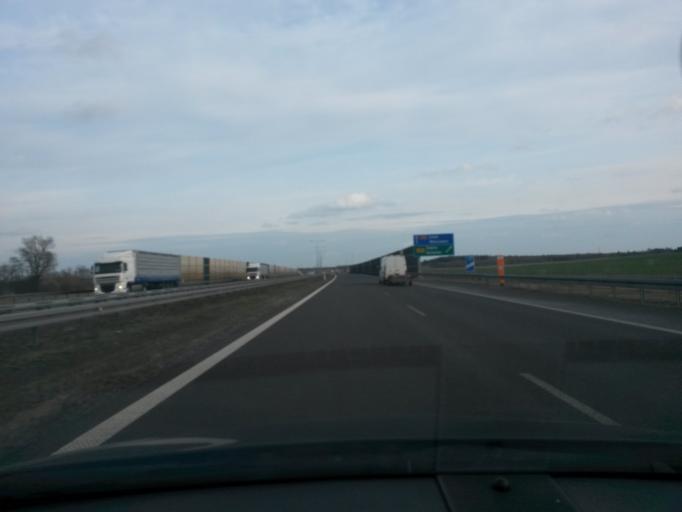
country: PL
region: Greater Poland Voivodeship
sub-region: Powiat kolski
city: Dabie
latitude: 52.0741
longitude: 18.8081
